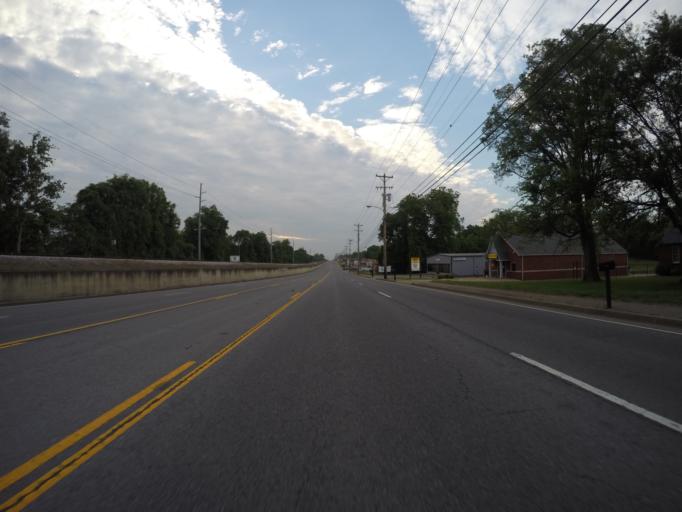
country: US
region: Tennessee
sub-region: Davidson County
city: Lakewood
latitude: 36.2402
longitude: -86.6318
